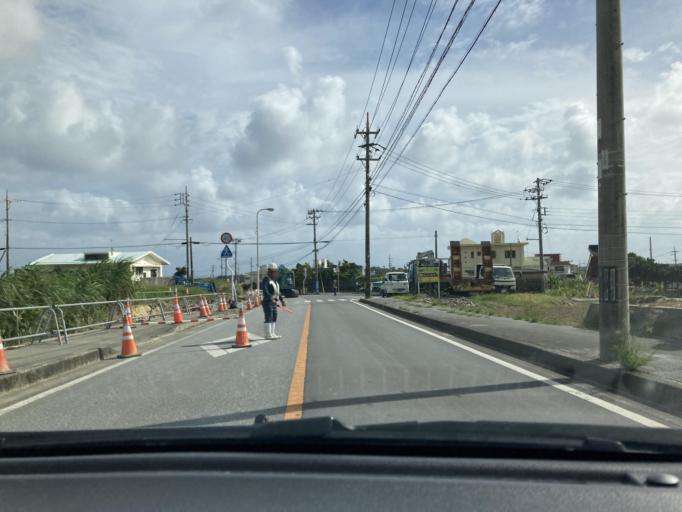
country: JP
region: Okinawa
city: Itoman
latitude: 26.1064
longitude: 127.6948
